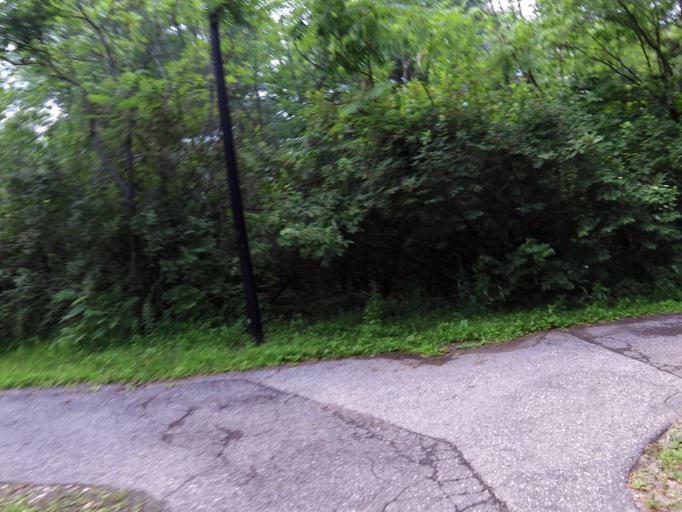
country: CA
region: Ontario
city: Bells Corners
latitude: 45.3050
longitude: -75.9068
